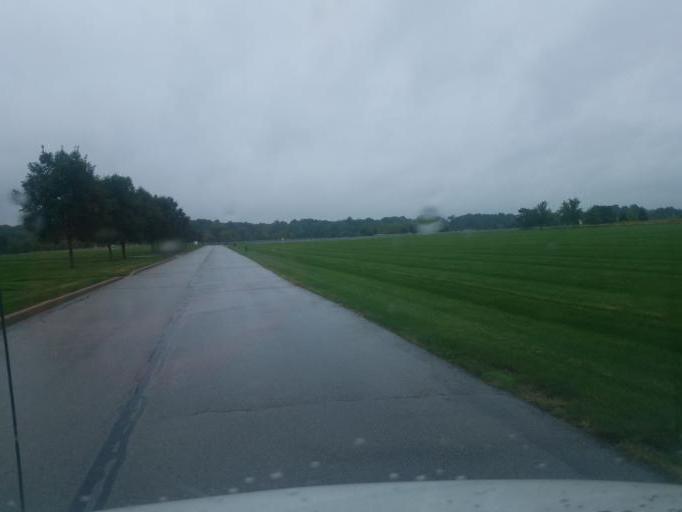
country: US
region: Ohio
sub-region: Wayne County
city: Rittman
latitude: 41.0031
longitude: -81.8120
